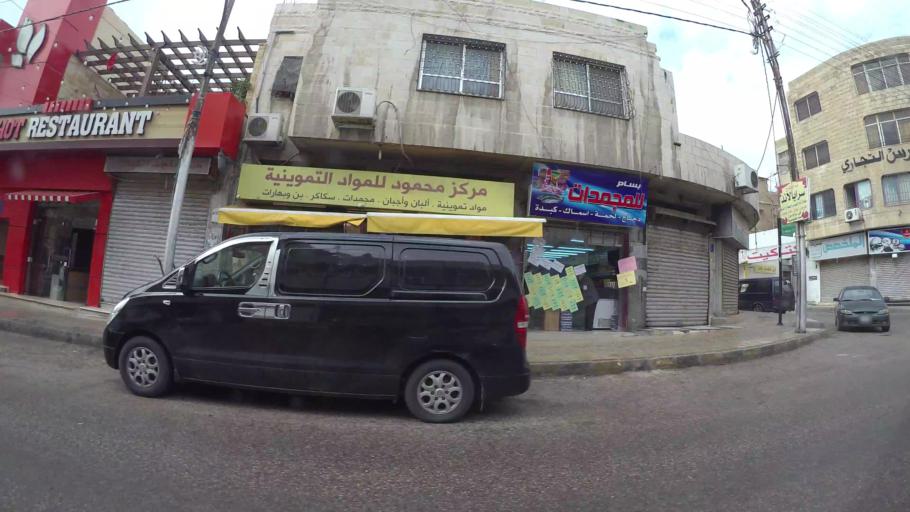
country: JO
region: Amman
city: Amman
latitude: 31.9752
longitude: 35.9255
